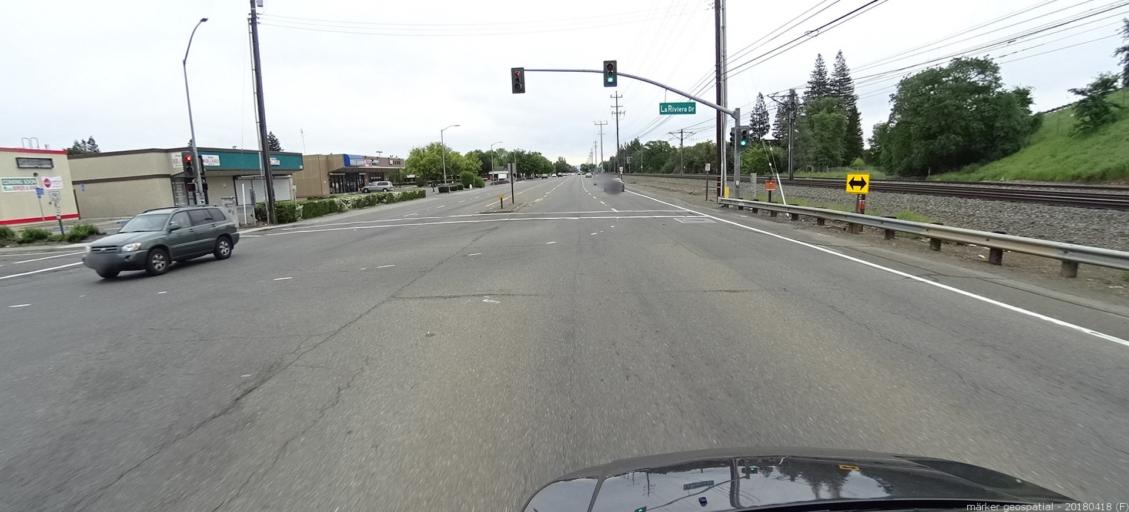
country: US
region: California
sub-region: Sacramento County
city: La Riviera
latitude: 38.5616
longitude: -121.3586
